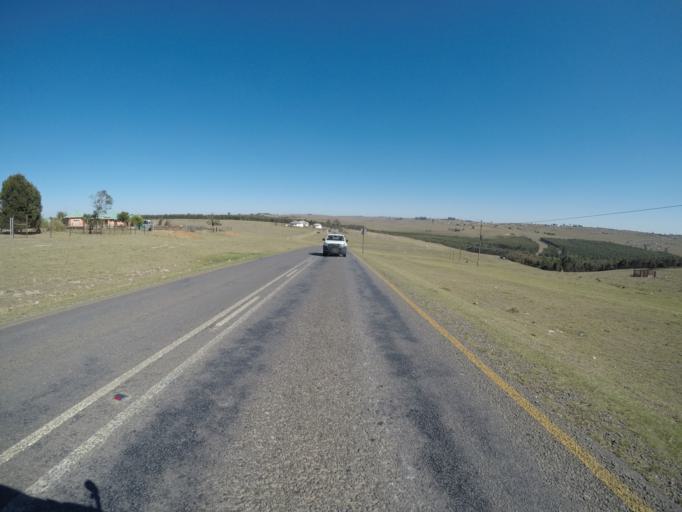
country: ZA
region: Eastern Cape
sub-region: OR Tambo District Municipality
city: Mthatha
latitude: -31.7825
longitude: 28.7393
